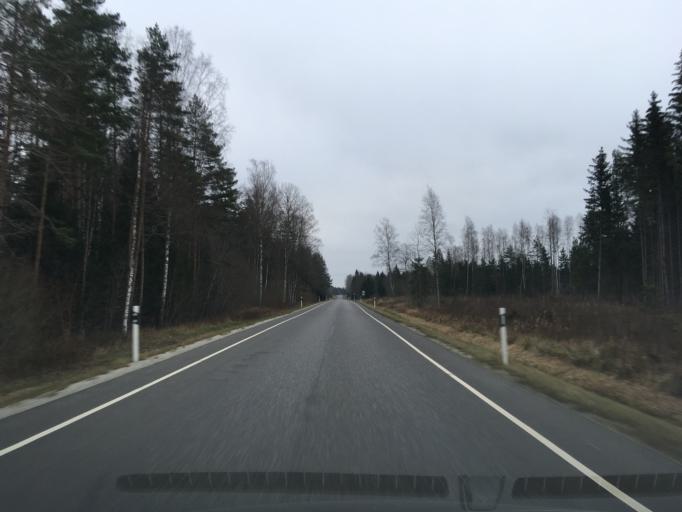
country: EE
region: Laeaene-Virumaa
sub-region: Tapa vald
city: Tapa
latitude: 59.4570
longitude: 25.9720
